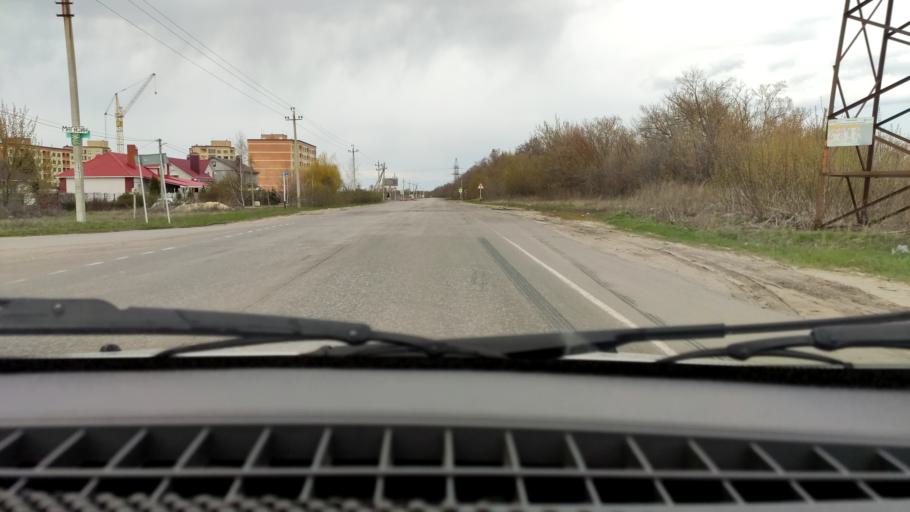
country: RU
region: Voronezj
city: Novaya Usman'
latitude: 51.6254
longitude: 39.3346
